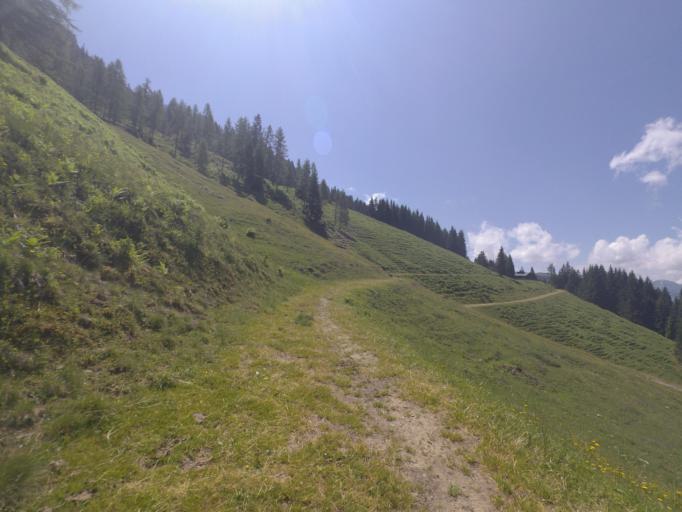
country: AT
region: Salzburg
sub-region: Politischer Bezirk Zell am See
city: Dienten am Hochkonig
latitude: 47.4186
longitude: 13.0025
